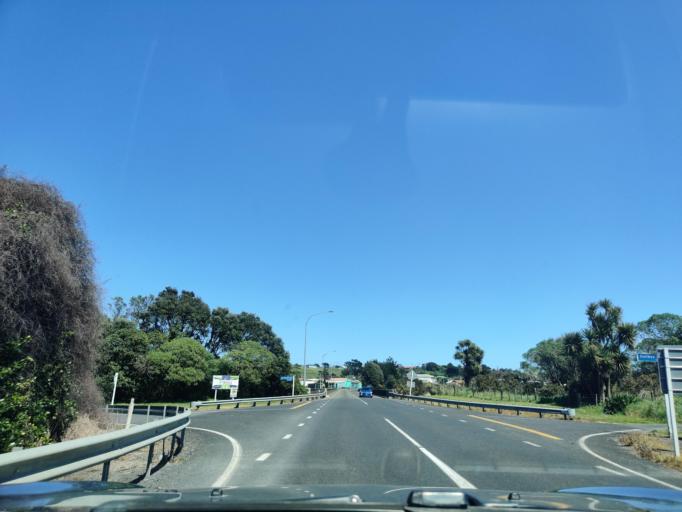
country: NZ
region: Taranaki
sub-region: South Taranaki District
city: Patea
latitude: -39.7560
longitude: 174.4860
